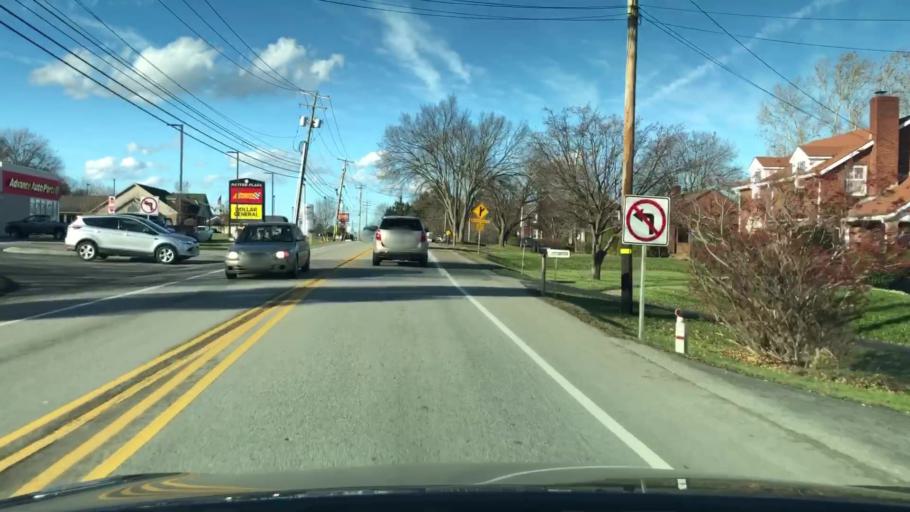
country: US
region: Pennsylvania
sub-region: Armstrong County
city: Freeport
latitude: 40.7038
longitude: -79.7227
